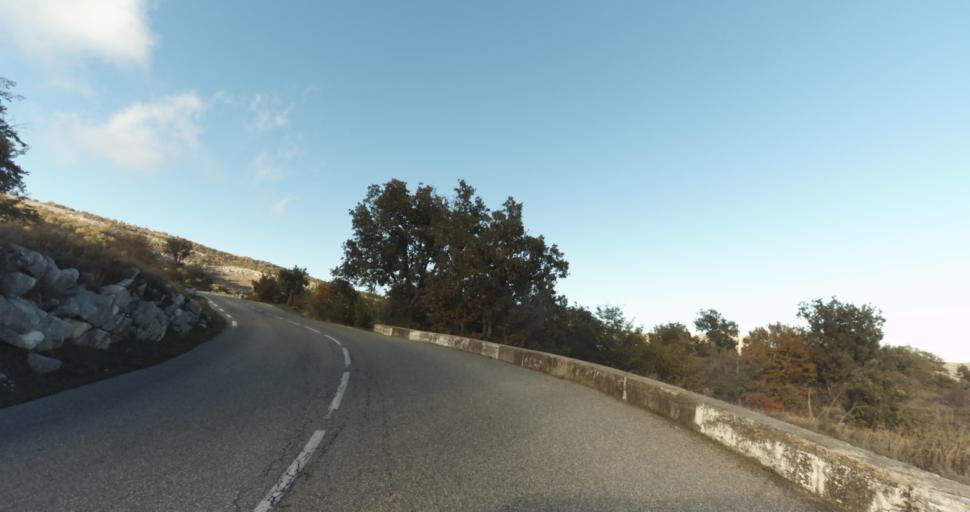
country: FR
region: Provence-Alpes-Cote d'Azur
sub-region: Departement des Alpes-Maritimes
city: Vence
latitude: 43.7625
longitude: 7.0854
